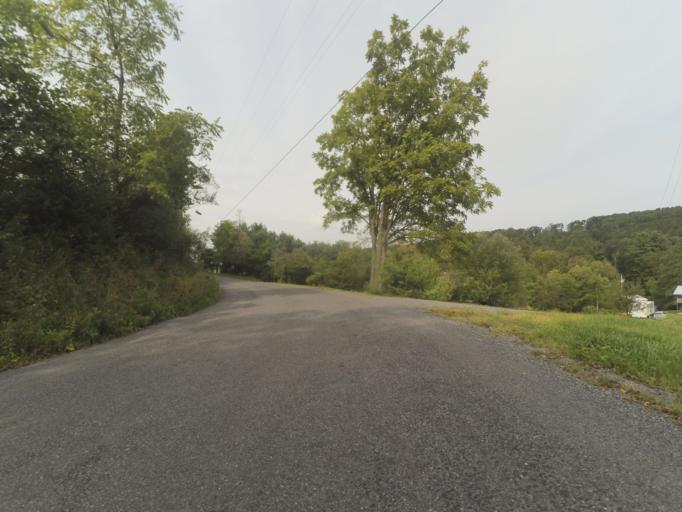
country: US
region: Pennsylvania
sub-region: Huntingdon County
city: Huntingdon
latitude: 40.6038
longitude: -78.0456
